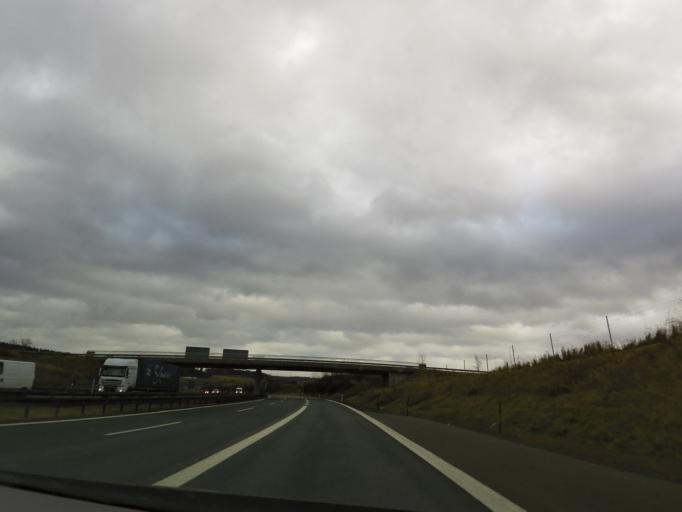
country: DE
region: Bavaria
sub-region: Upper Franconia
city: Trogen
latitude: 50.3794
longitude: 11.9636
